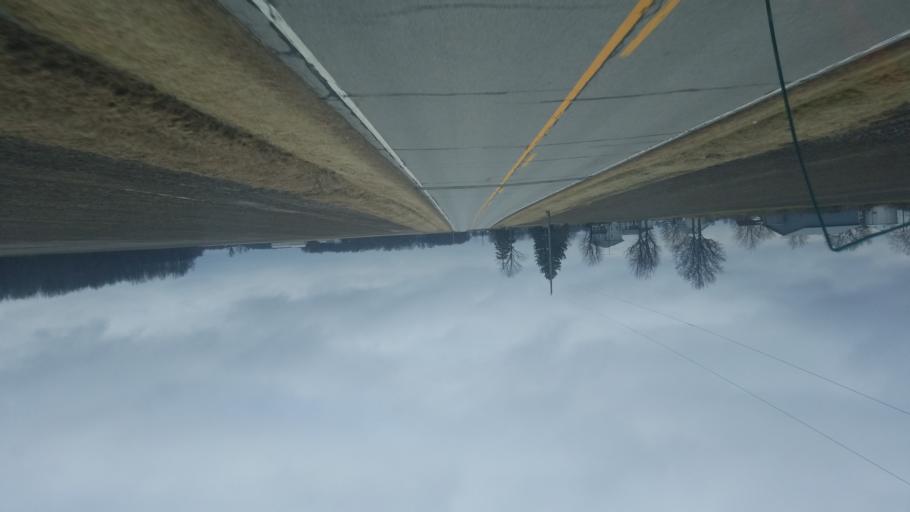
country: US
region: Ohio
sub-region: Crawford County
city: Bucyrus
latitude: 40.7207
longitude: -82.9529
